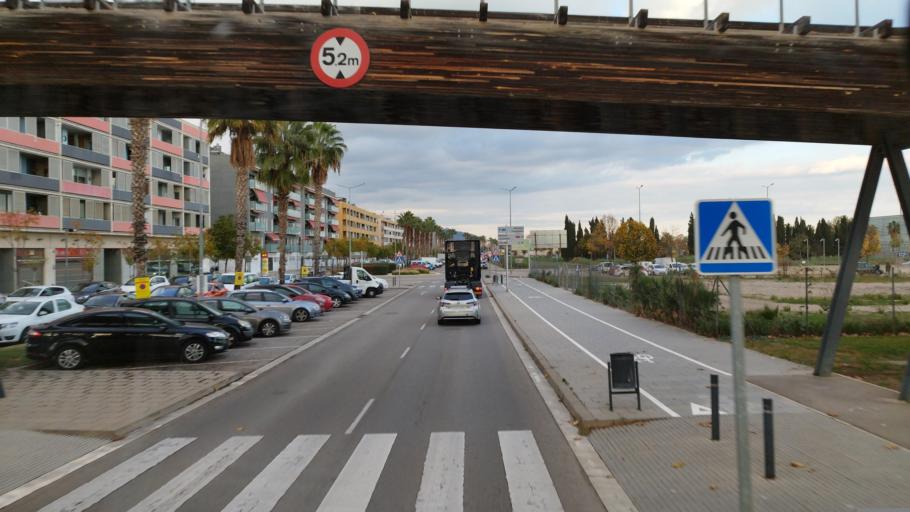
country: ES
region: Catalonia
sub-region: Provincia de Barcelona
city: Viladecans
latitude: 41.3141
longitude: 2.0271
